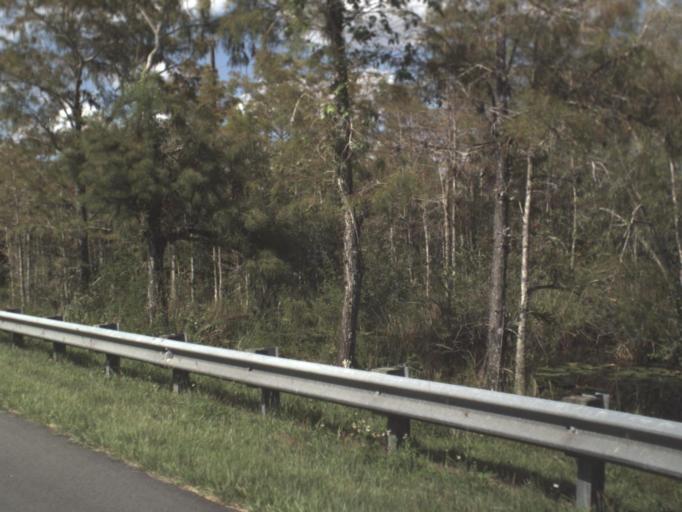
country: US
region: Florida
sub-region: Miami-Dade County
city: Kendall West
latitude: 25.8353
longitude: -80.9078
